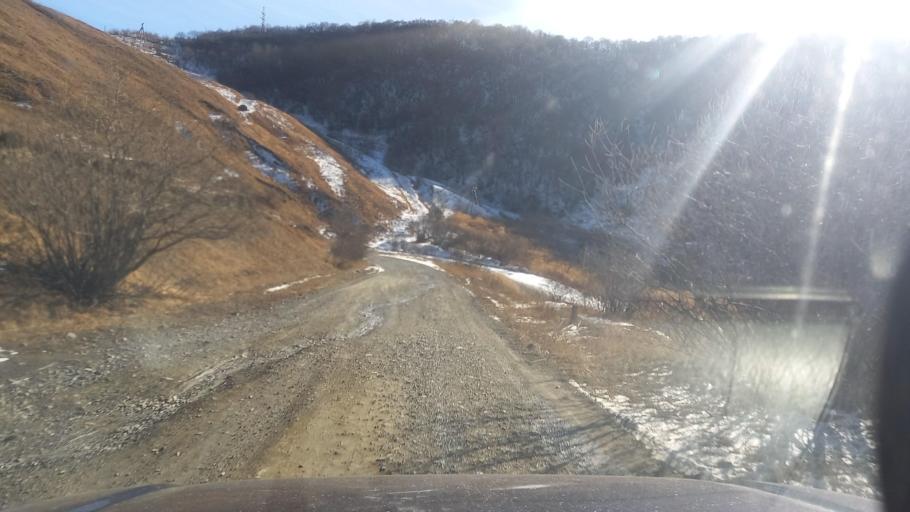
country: RU
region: North Ossetia
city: Verkhniy Fiagdon
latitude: 42.8357
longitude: 44.4728
